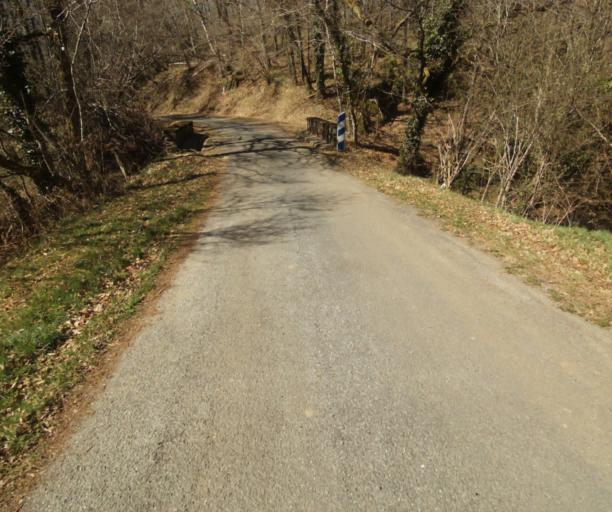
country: FR
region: Limousin
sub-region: Departement de la Correze
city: Uzerche
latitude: 45.4093
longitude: 1.6088
